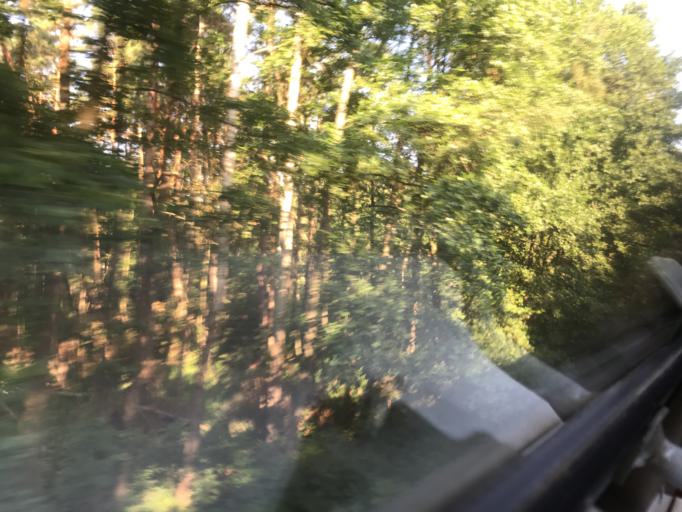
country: CZ
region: Jihocesky
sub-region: Okres Jindrichuv Hradec
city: Lomnice nad Luznici
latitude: 49.1392
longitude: 14.7368
